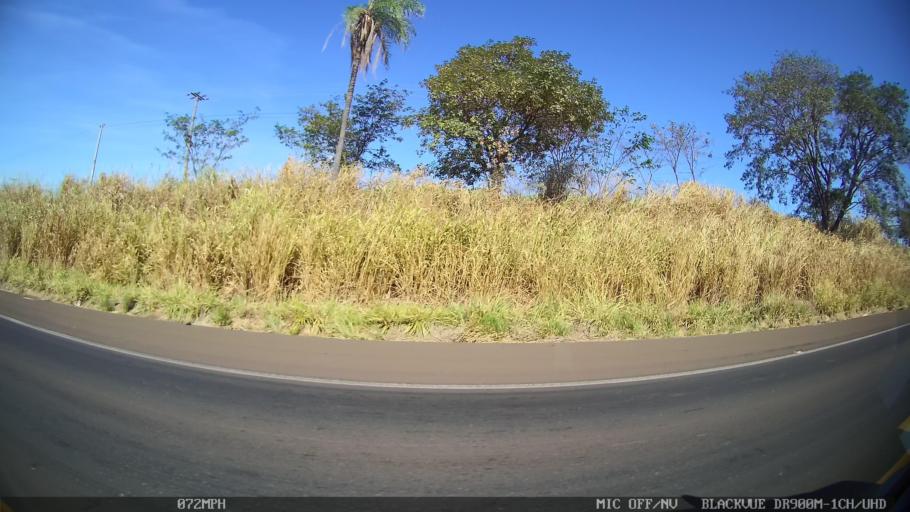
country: BR
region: Sao Paulo
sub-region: Olimpia
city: Olimpia
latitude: -20.6357
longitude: -48.8190
